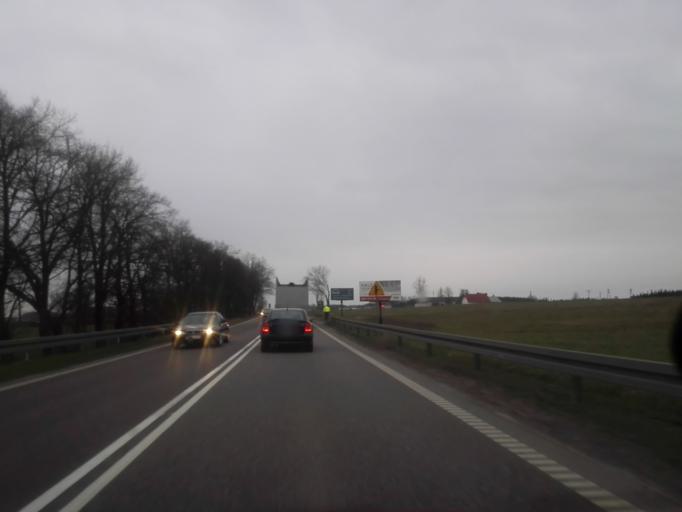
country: PL
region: Podlasie
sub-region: Powiat grajewski
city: Grajewo
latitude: 53.6276
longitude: 22.4115
